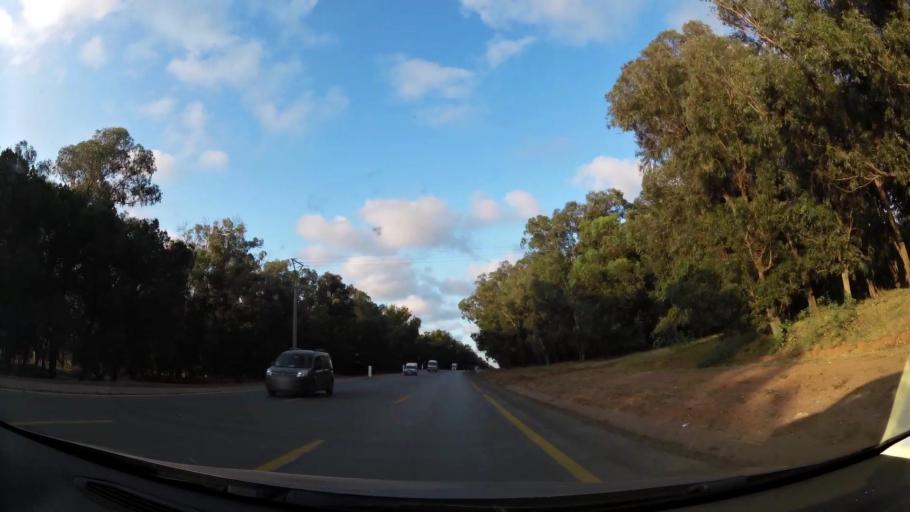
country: MA
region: Gharb-Chrarda-Beni Hssen
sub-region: Kenitra Province
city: Kenitra
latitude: 34.2301
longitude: -6.6457
